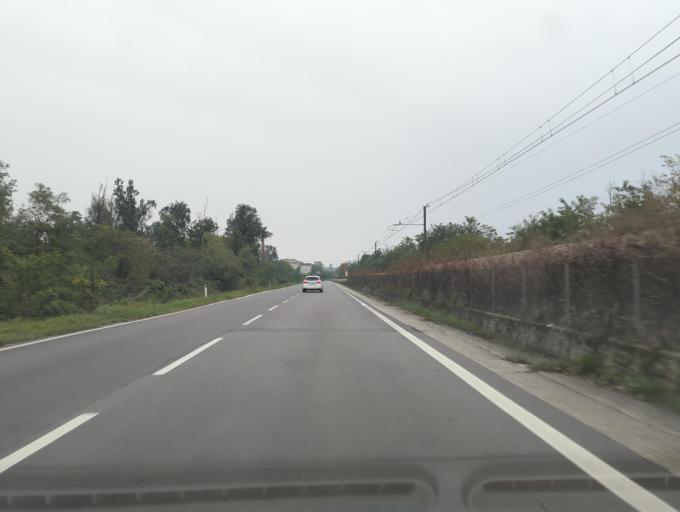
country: IT
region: Lombardy
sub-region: Citta metropolitana di Milano
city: Turbigo
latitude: 45.5136
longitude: 8.7243
